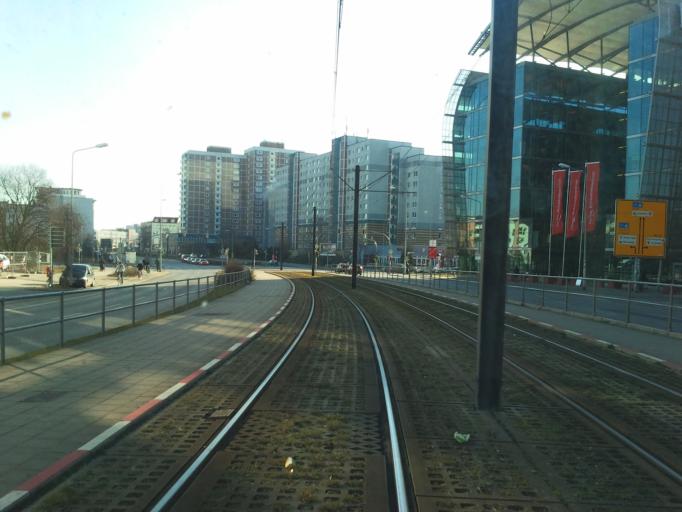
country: DE
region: Mecklenburg-Vorpommern
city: Rostock
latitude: 54.0867
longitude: 12.1262
